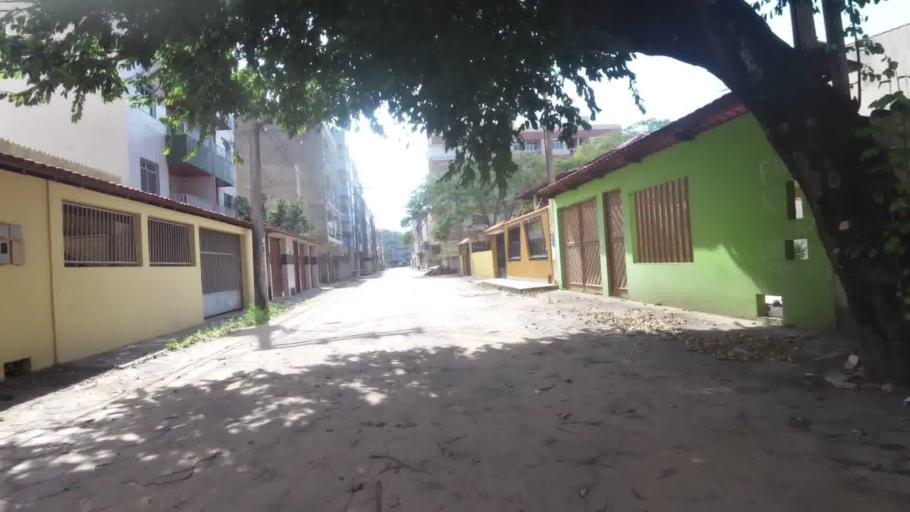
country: BR
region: Espirito Santo
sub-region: Piuma
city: Piuma
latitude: -20.8479
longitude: -40.7453
